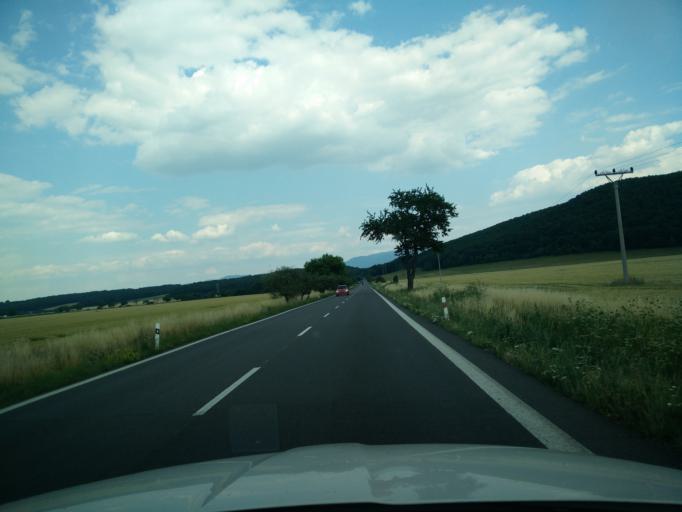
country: SK
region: Nitriansky
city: Novaky
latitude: 48.7230
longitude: 18.4857
